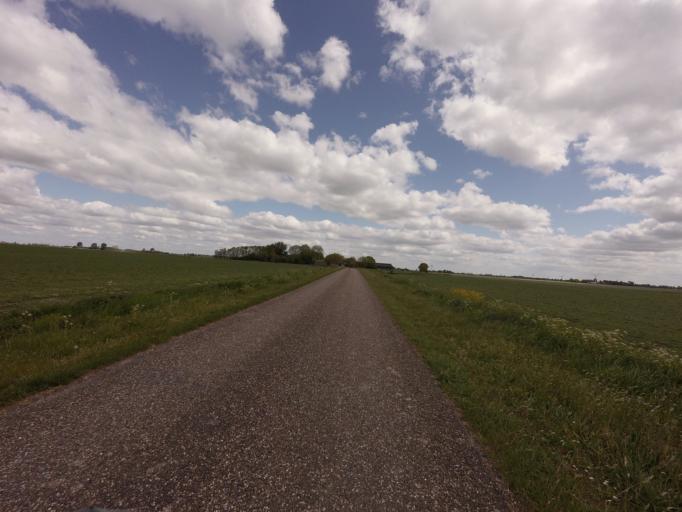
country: NL
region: Friesland
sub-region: Gemeente Franekeradeel
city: Tzum
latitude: 53.1355
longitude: 5.5606
